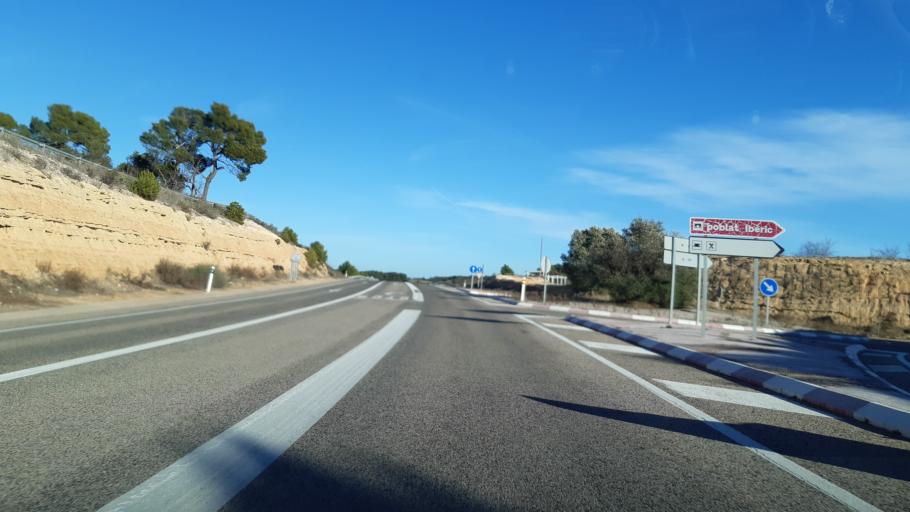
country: ES
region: Catalonia
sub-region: Provincia de Tarragona
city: Bot
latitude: 41.0486
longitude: 0.3752
